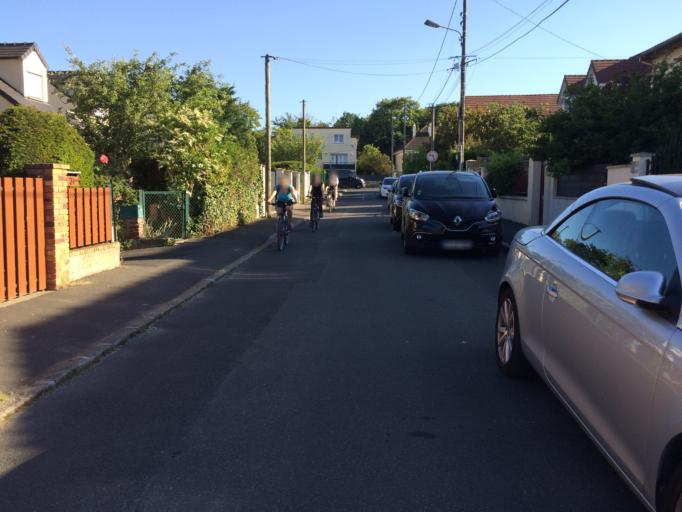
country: FR
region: Ile-de-France
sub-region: Departement de l'Essonne
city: Igny
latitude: 48.7263
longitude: 2.2212
